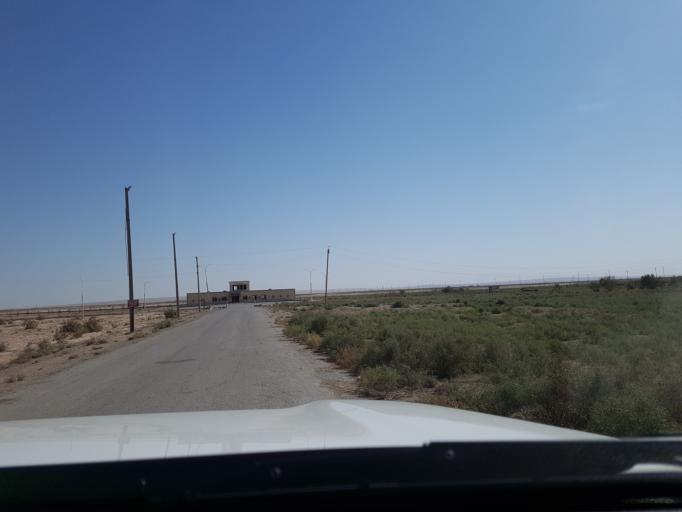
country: IR
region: Razavi Khorasan
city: Sarakhs
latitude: 36.4932
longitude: 61.2545
